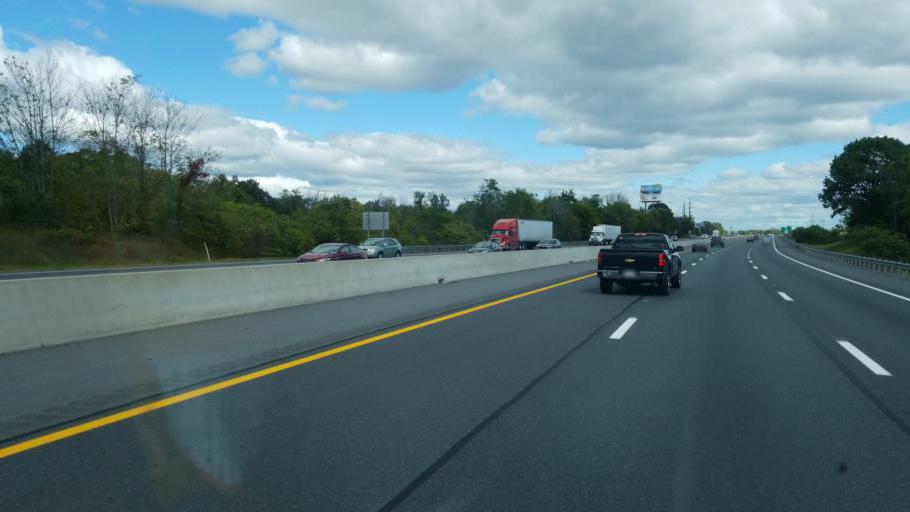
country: US
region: West Virginia
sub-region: Berkeley County
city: Martinsburg
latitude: 39.5272
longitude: -77.9270
